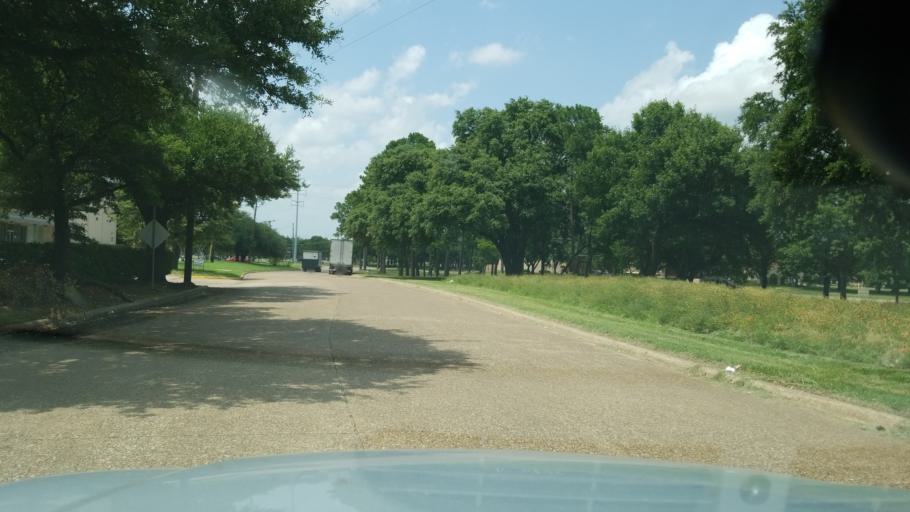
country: US
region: Texas
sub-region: Dallas County
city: University Park
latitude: 32.8302
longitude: -96.8598
